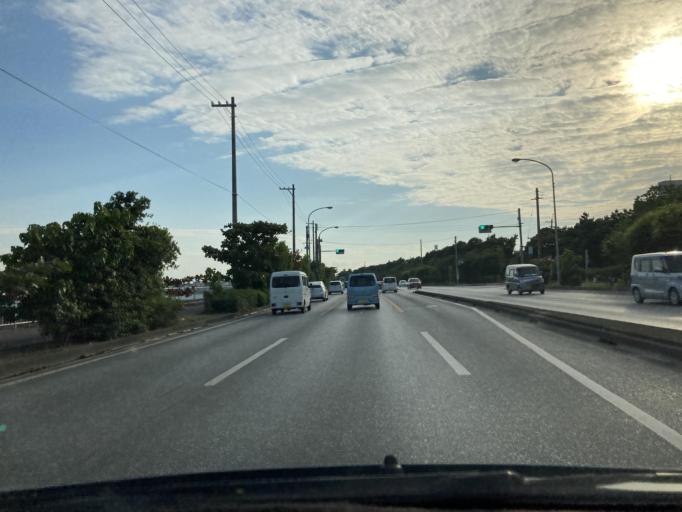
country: JP
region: Okinawa
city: Okinawa
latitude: 26.3293
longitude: 127.8362
